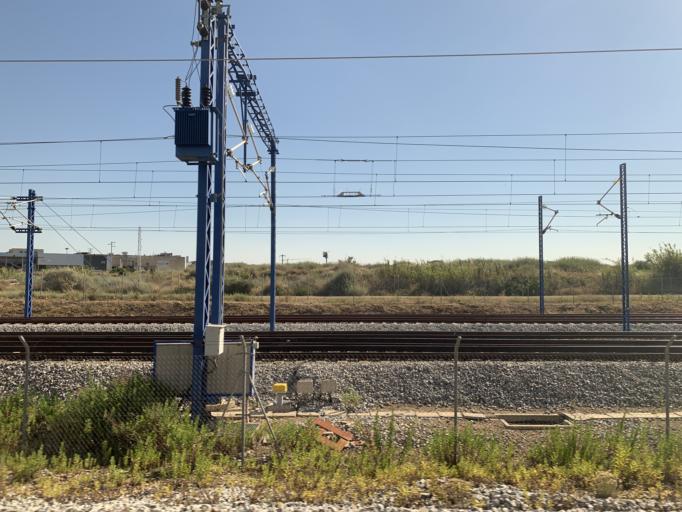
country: ES
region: Aragon
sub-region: Provincia de Zaragoza
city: Almozara
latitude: 41.6636
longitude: -0.9210
